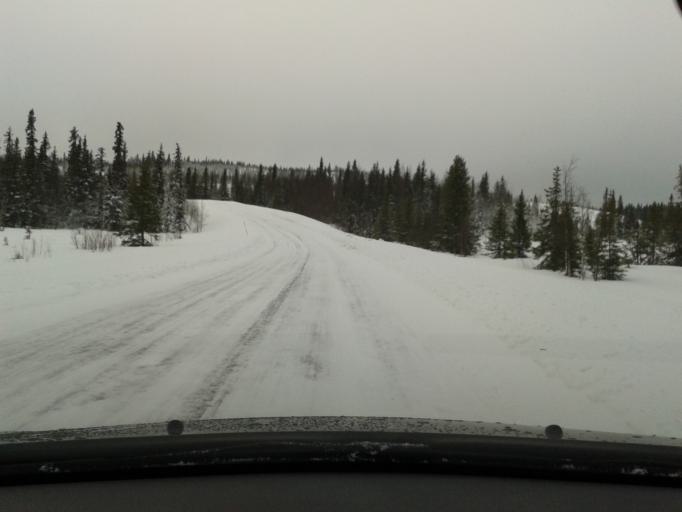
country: SE
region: Vaesterbotten
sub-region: Vilhelmina Kommun
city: Sjoberg
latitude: 65.2054
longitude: 15.9825
